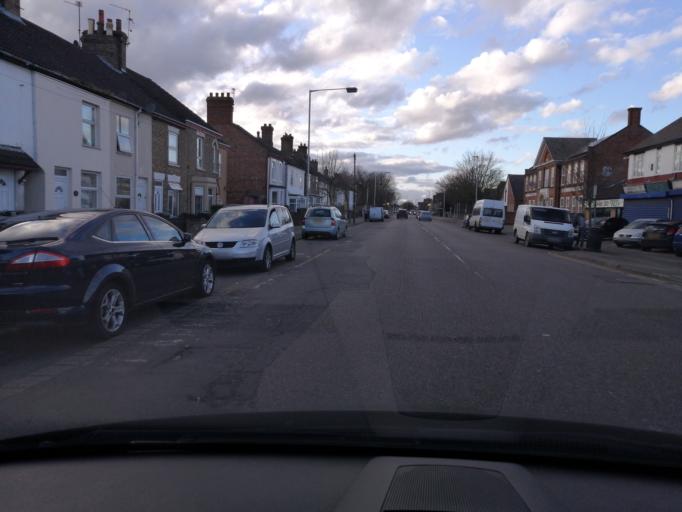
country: GB
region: England
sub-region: Peterborough
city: Peterborough
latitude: 52.5893
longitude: -0.2497
